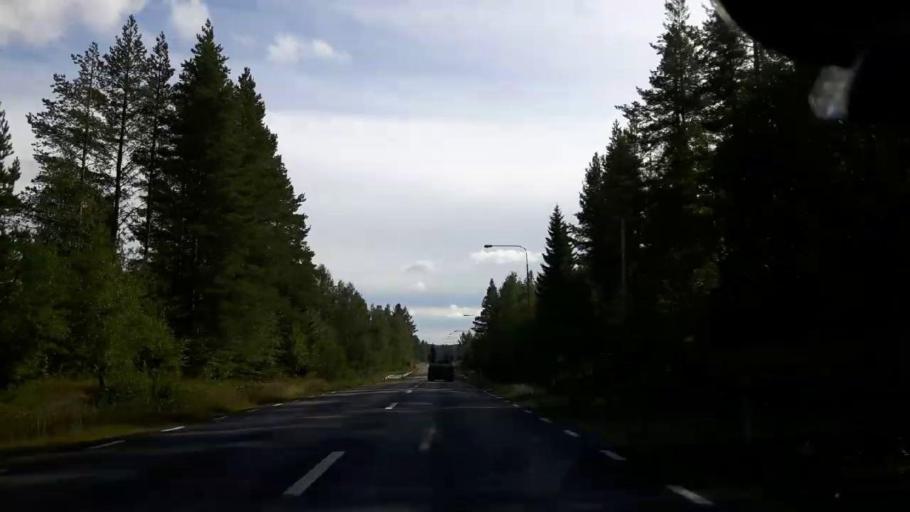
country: SE
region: Jaemtland
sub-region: Braecke Kommun
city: Braecke
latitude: 63.1769
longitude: 15.5284
